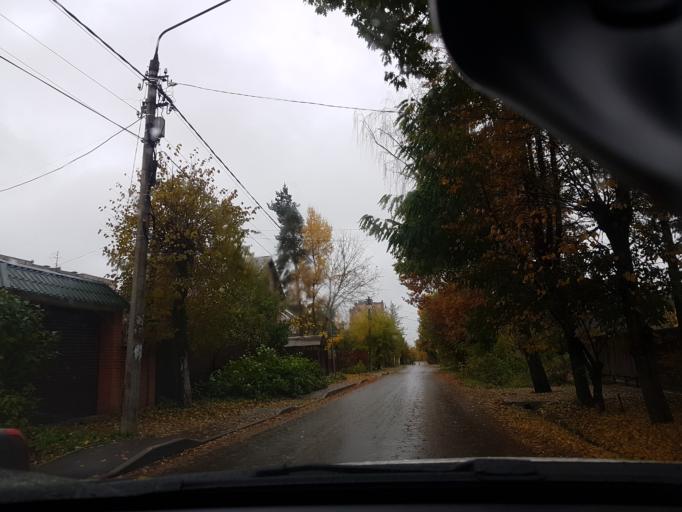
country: RU
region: Moskovskaya
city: Istra
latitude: 55.9180
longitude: 36.8754
